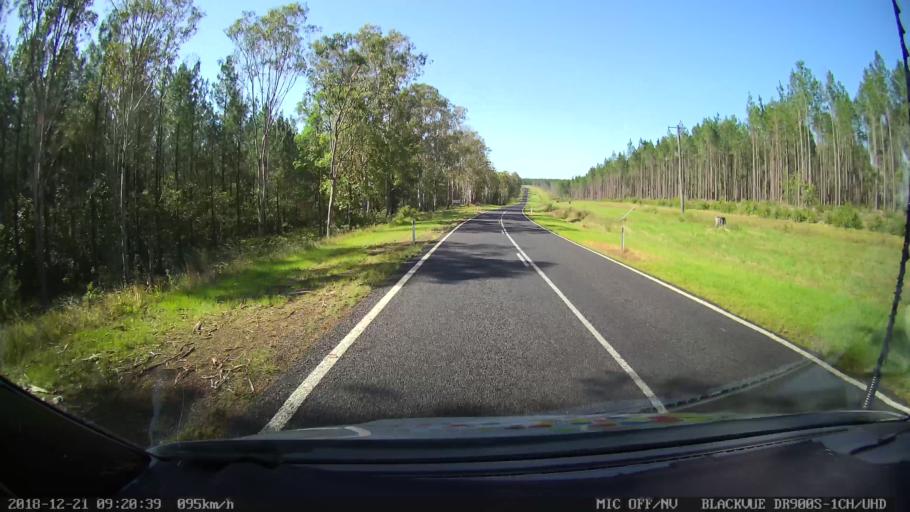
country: AU
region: New South Wales
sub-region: Clarence Valley
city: Maclean
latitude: -29.3175
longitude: 153.0002
